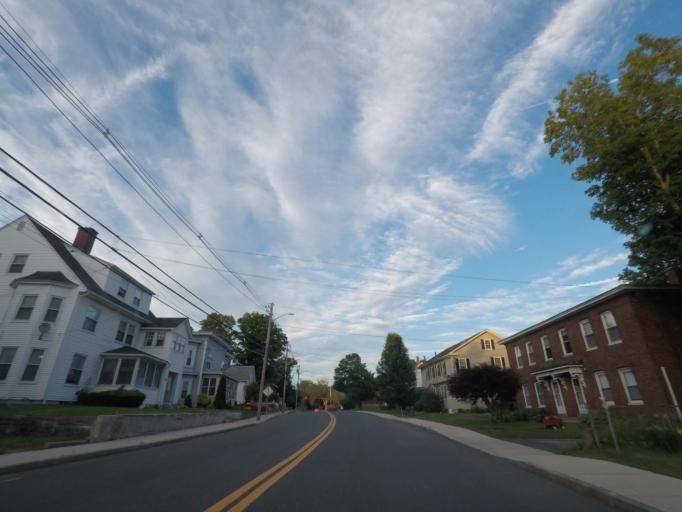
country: US
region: Massachusetts
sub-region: Worcester County
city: Warren
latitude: 42.2119
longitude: -72.2370
